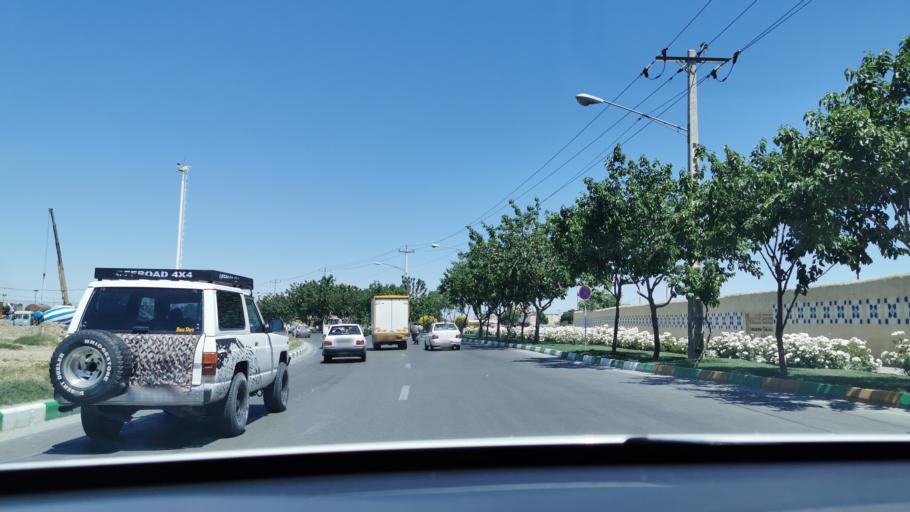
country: IR
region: Razavi Khorasan
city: Mashhad
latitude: 36.2592
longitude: 59.6456
